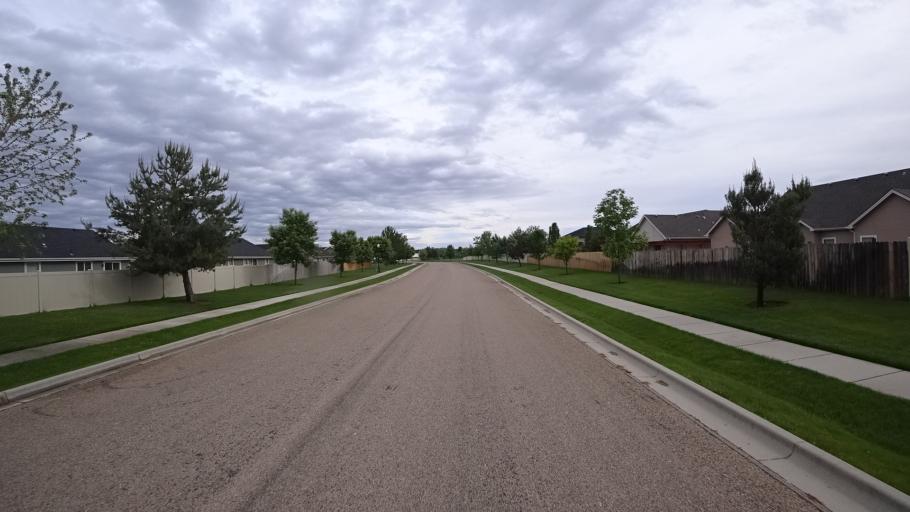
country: US
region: Idaho
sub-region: Ada County
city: Star
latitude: 43.6986
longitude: -116.5051
